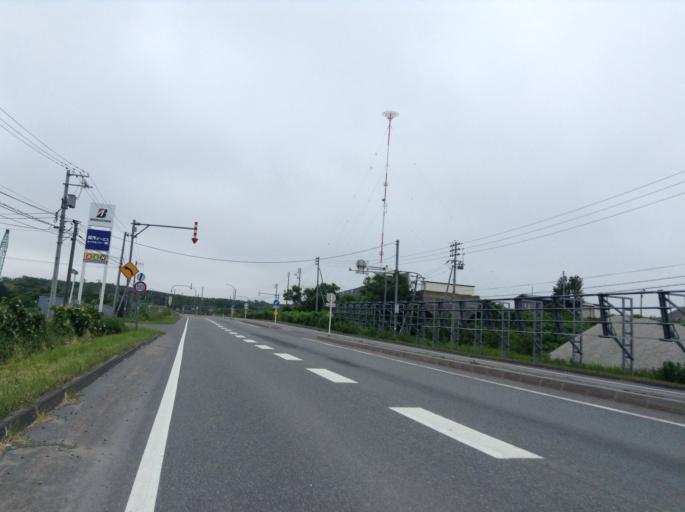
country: JP
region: Hokkaido
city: Wakkanai
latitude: 45.3778
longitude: 141.7113
